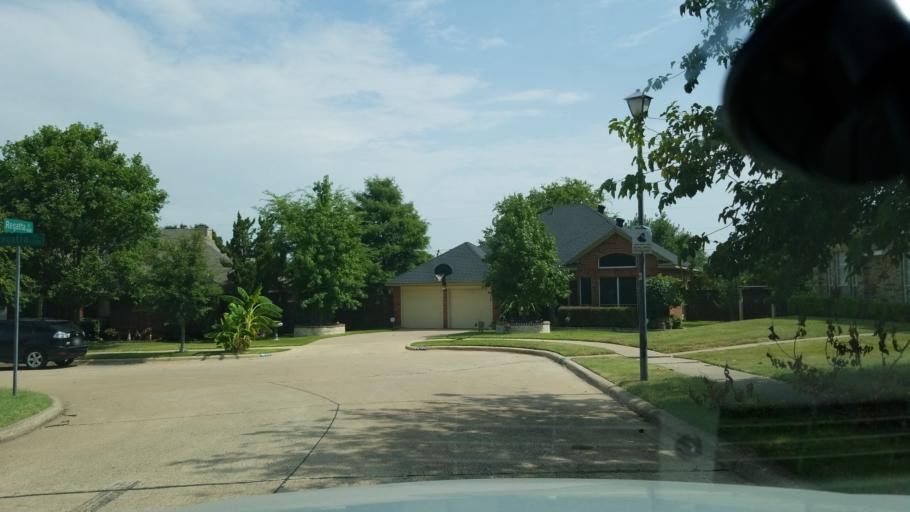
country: US
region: Texas
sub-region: Dallas County
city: Cockrell Hill
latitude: 32.6879
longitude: -96.8438
